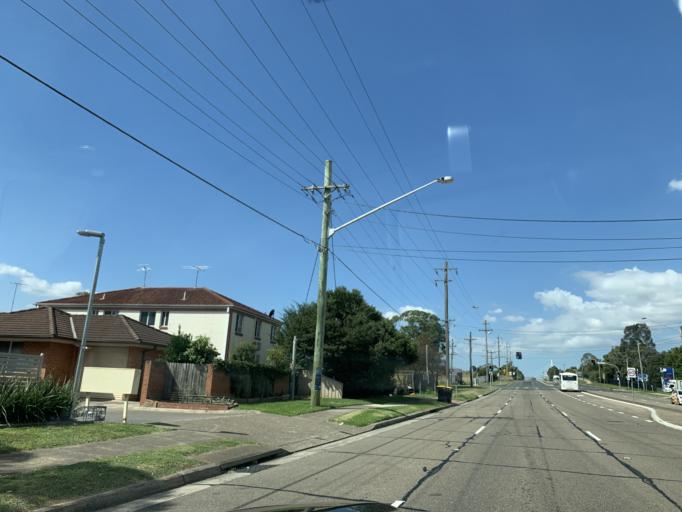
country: AU
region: New South Wales
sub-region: Penrith Municipality
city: Werrington County
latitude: -33.7618
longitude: 150.7337
